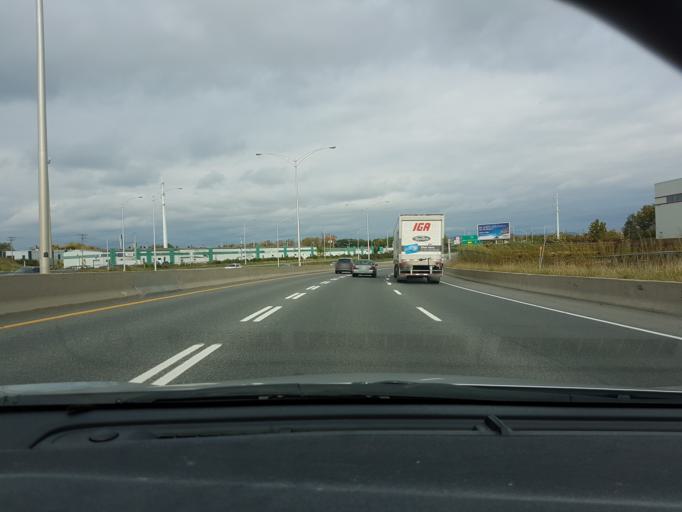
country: CA
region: Quebec
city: L'Ancienne-Lorette
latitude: 46.8038
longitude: -71.2892
